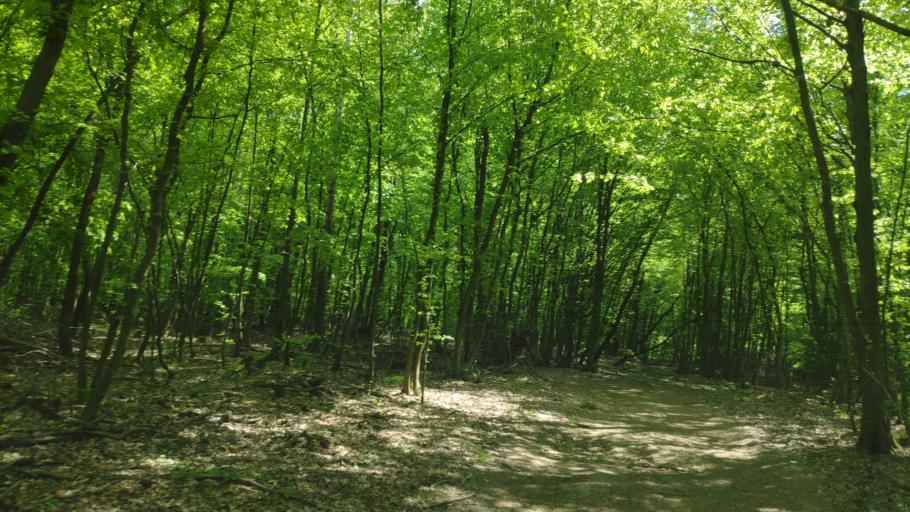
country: SK
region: Kosicky
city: Kosice
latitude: 48.6640
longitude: 21.4309
